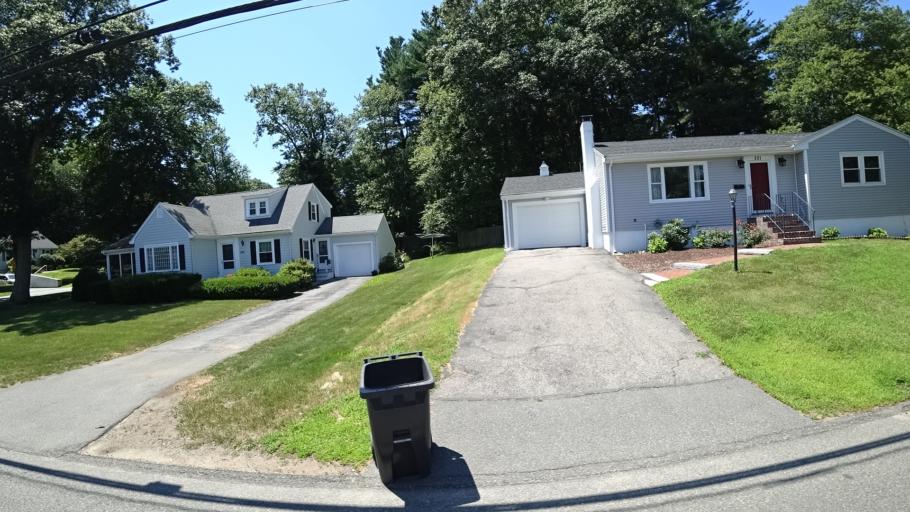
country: US
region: Massachusetts
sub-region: Norfolk County
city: Dedham
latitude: 42.2373
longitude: -71.1838
